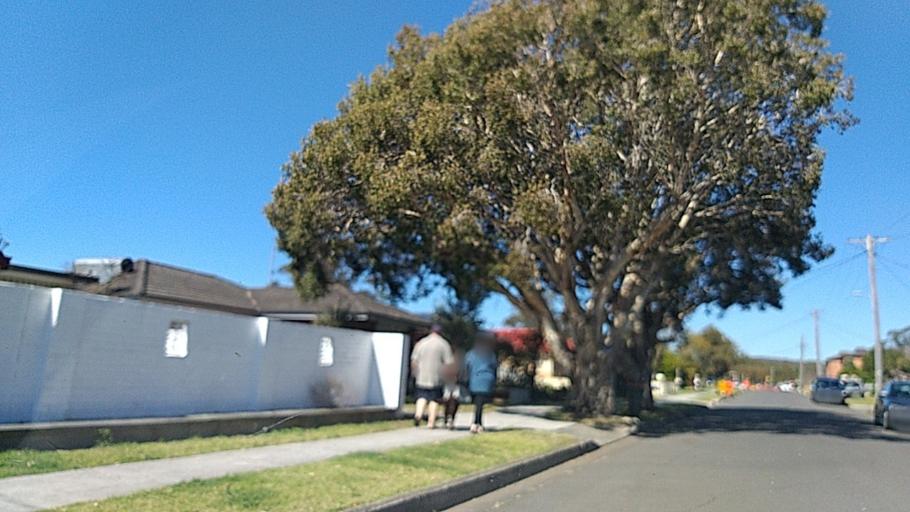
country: AU
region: New South Wales
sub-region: Wollongong
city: Koonawarra
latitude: -34.4836
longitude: 150.8067
